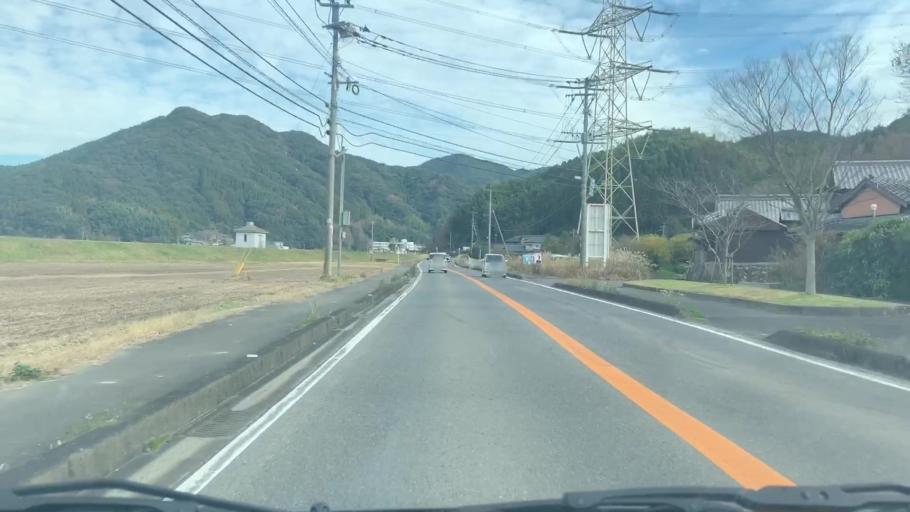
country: JP
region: Saga Prefecture
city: Karatsu
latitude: 33.3572
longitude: 130.0062
